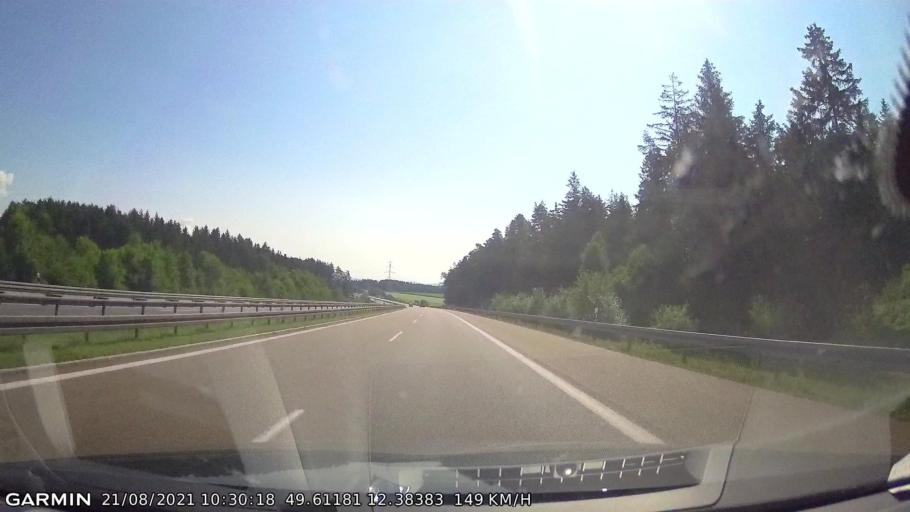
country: DE
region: Bavaria
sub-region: Upper Palatinate
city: Moosbach
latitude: 49.6115
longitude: 12.3847
